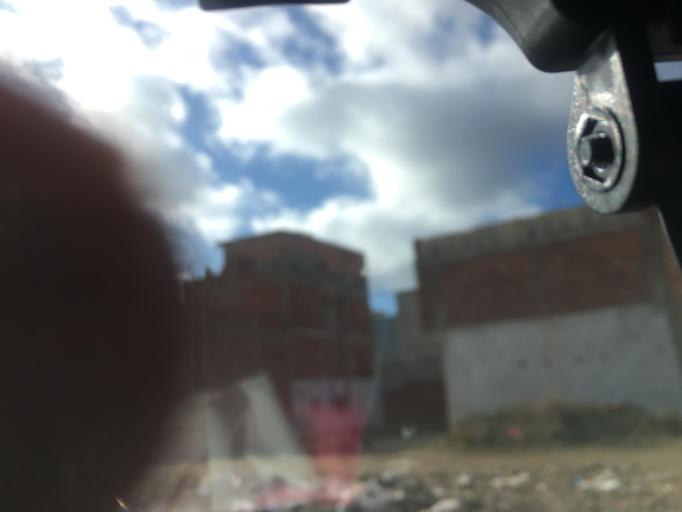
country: MA
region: Tanger-Tetouan
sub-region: Tanger-Assilah
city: Tangier
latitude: 35.7124
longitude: -5.8141
